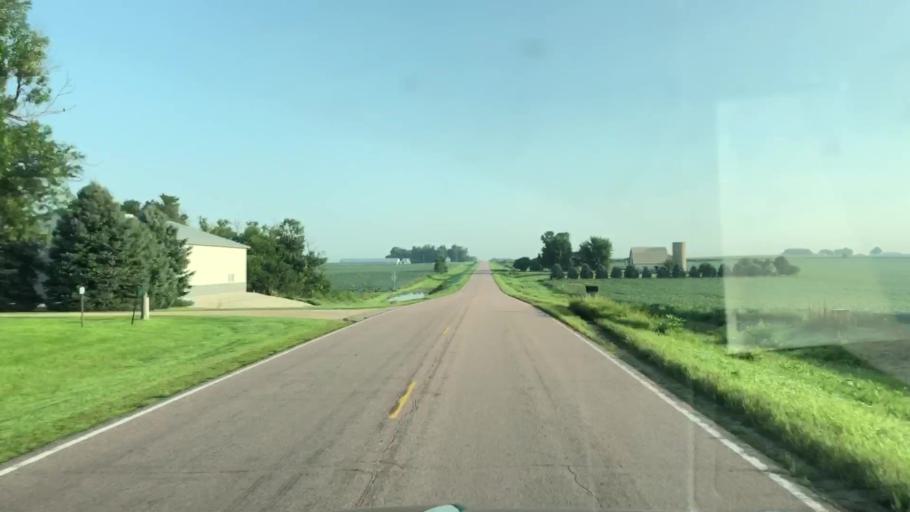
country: US
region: Iowa
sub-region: Lyon County
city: George
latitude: 43.2735
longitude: -95.9998
